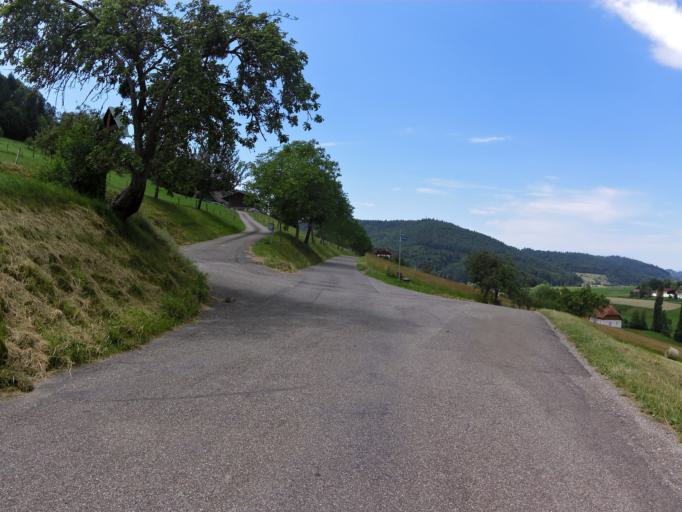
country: DE
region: Baden-Wuerttemberg
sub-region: Freiburg Region
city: Seelbach
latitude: 48.3215
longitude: 7.9528
